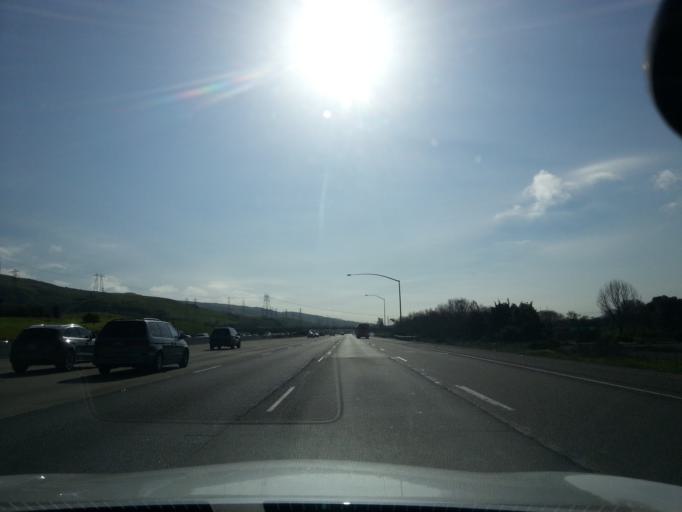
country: US
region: California
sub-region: Santa Clara County
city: Seven Trees
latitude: 37.2331
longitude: -121.7539
